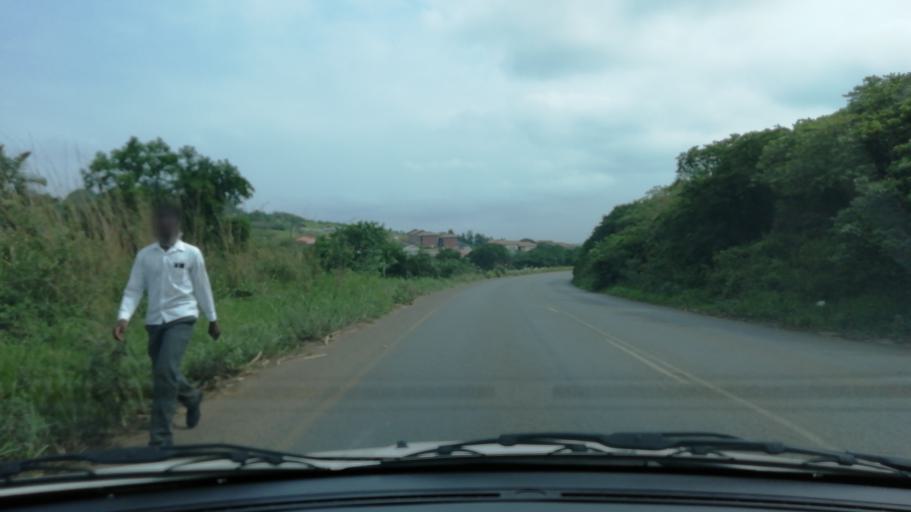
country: ZA
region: KwaZulu-Natal
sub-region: uThungulu District Municipality
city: Empangeni
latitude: -28.7471
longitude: 31.8806
